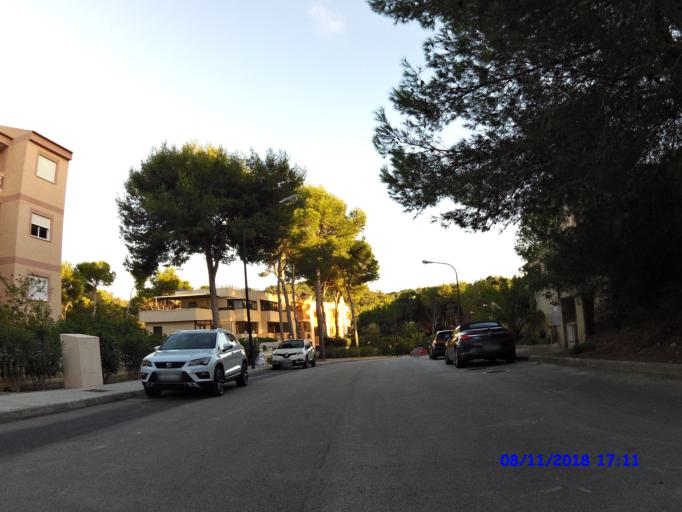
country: ES
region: Balearic Islands
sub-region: Illes Balears
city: Santa Ponsa
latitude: 39.5338
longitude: 2.4626
